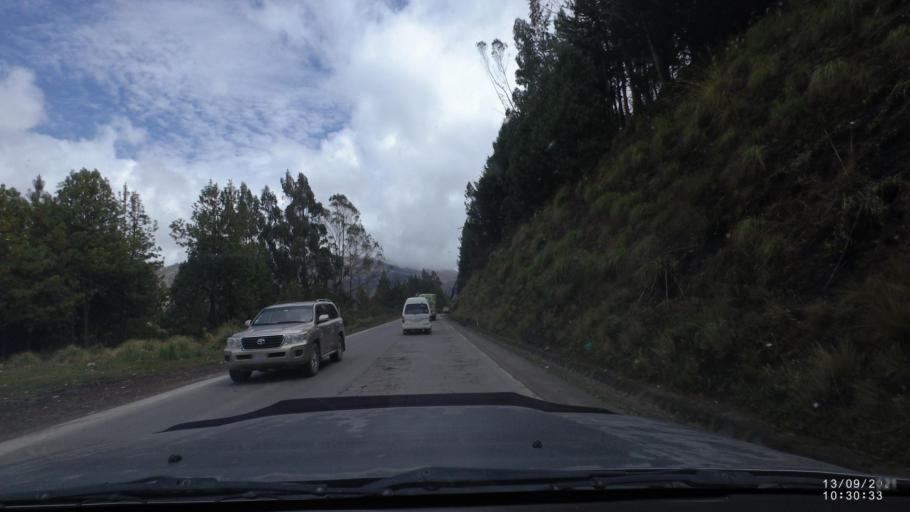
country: BO
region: Cochabamba
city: Colomi
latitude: -17.2615
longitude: -65.8877
